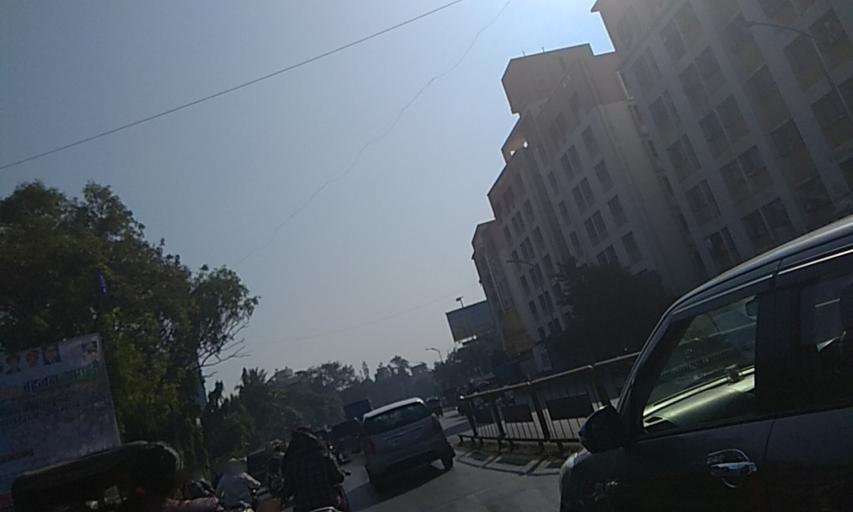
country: IN
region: Maharashtra
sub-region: Pune Division
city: Pune
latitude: 18.5012
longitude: 73.8471
